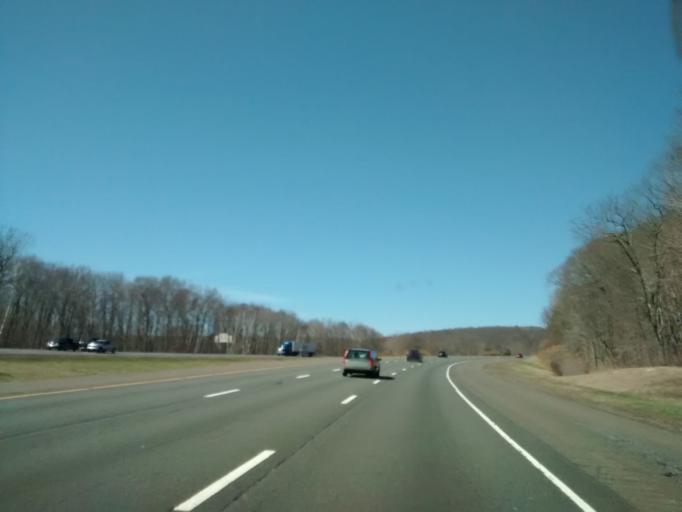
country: US
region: Connecticut
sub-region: Tolland County
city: Tolland
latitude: 41.8541
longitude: -72.3869
